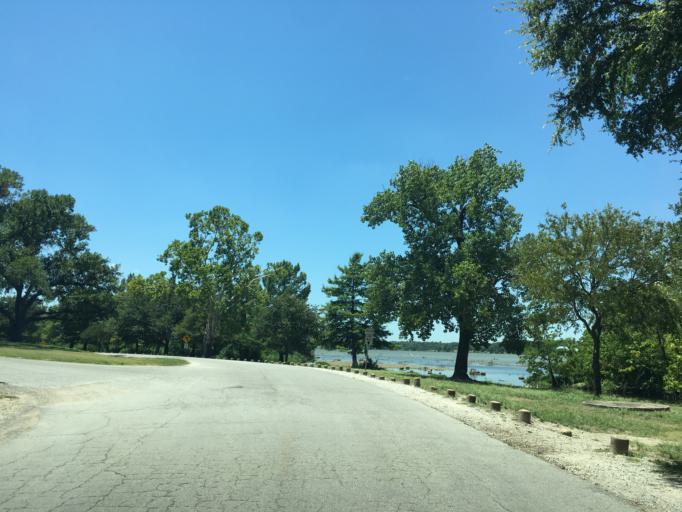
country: US
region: Texas
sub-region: Dallas County
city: Highland Park
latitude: 32.8340
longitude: -96.7110
